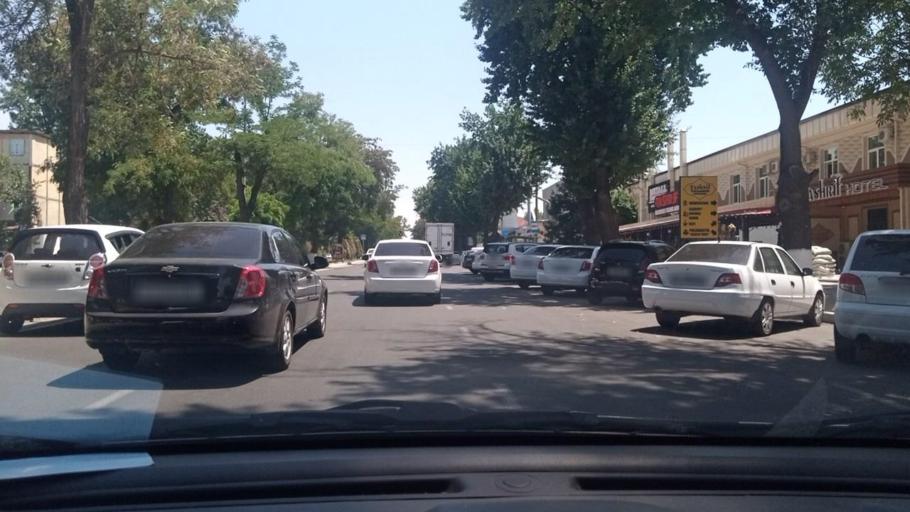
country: UZ
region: Toshkent Shahri
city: Tashkent
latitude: 41.2930
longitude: 69.1984
